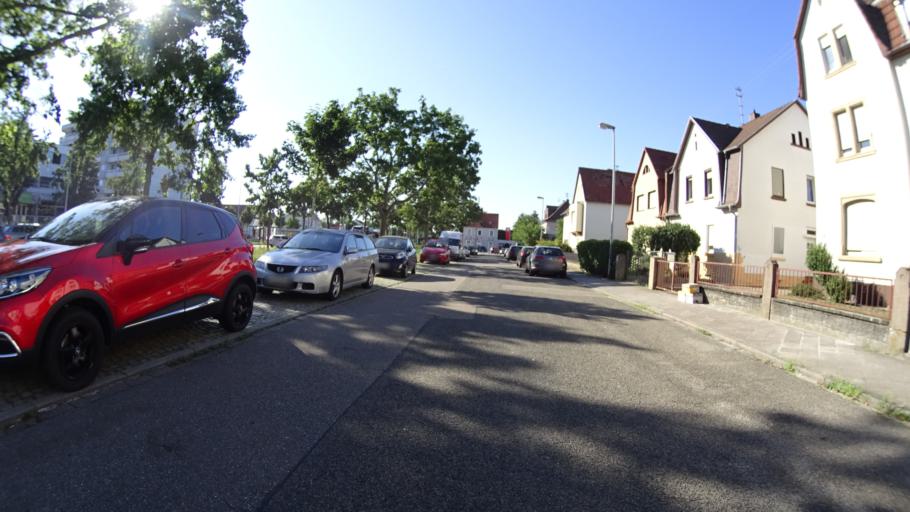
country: DE
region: Baden-Wuerttemberg
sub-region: Karlsruhe Region
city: Karlsruhe
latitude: 49.0302
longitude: 8.3421
